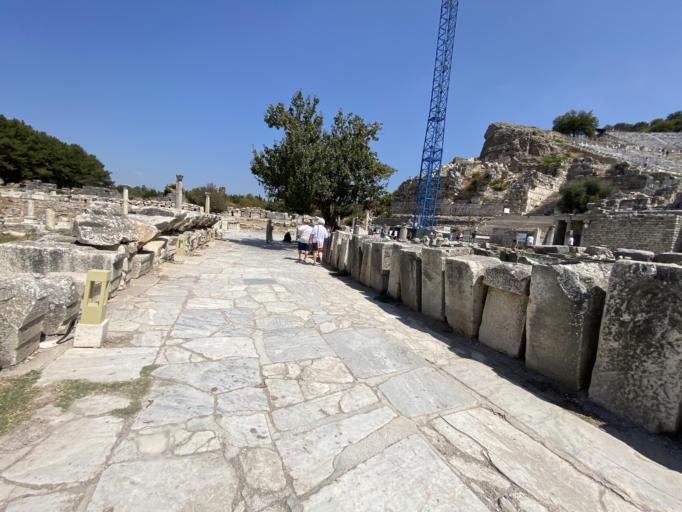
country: TR
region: Izmir
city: Selcuk
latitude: 37.9413
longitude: 27.3417
